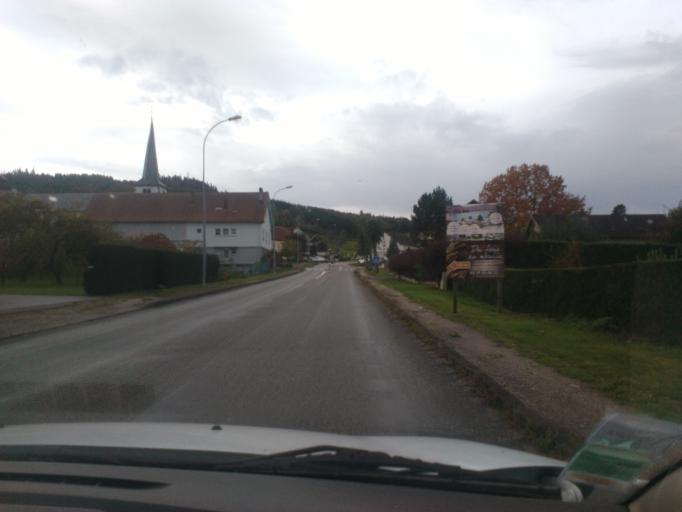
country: FR
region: Lorraine
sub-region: Departement des Vosges
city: Anould
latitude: 48.1510
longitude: 6.9213
